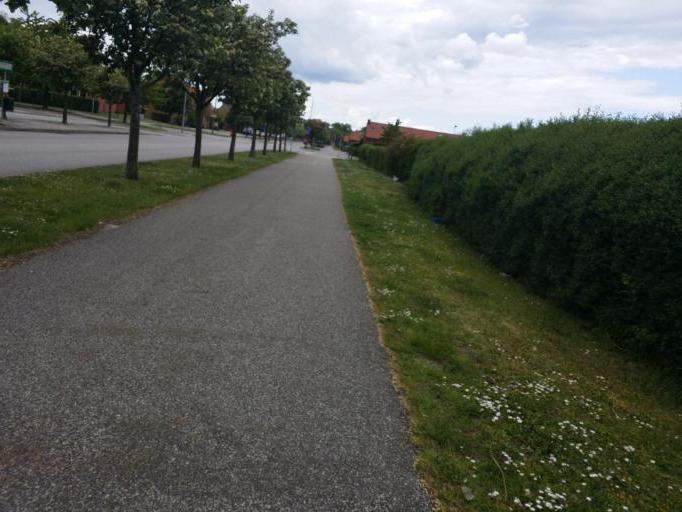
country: SE
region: Skane
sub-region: Burlovs Kommun
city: Arloev
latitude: 55.6006
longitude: 13.0858
